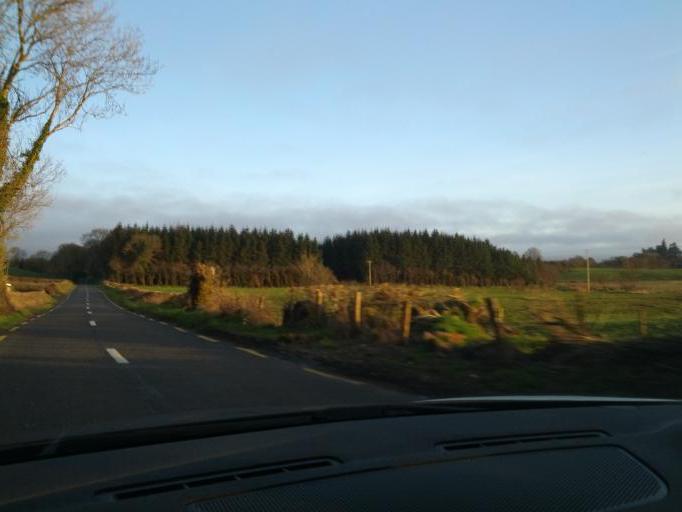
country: IE
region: Connaught
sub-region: Sligo
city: Tobercurry
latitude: 54.0407
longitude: -8.6221
